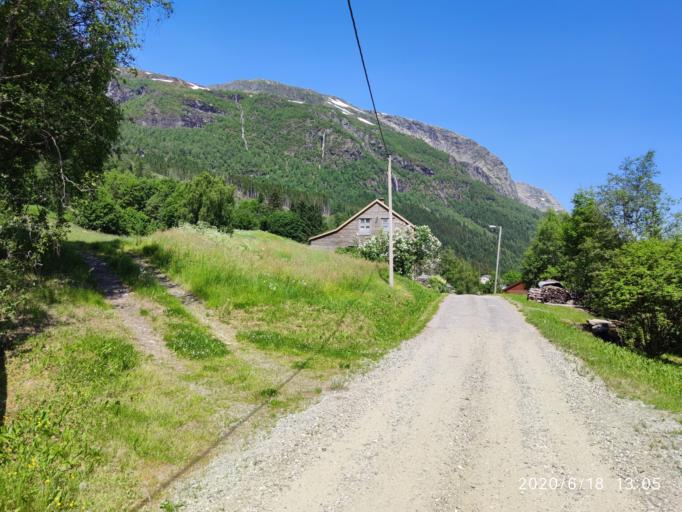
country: NO
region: Hordaland
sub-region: Voss
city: Voss
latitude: 60.6598
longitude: 6.4215
